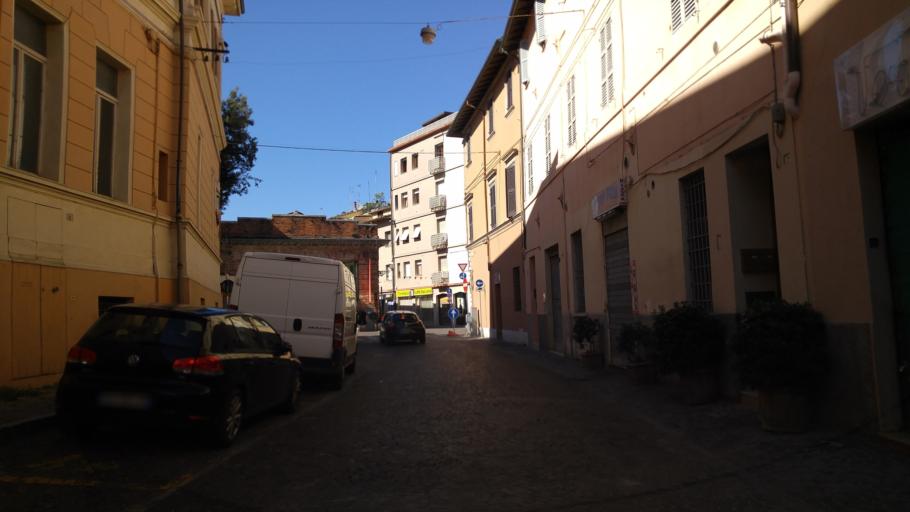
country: IT
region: The Marches
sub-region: Provincia di Pesaro e Urbino
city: Pesaro
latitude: 43.9115
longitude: 12.9082
